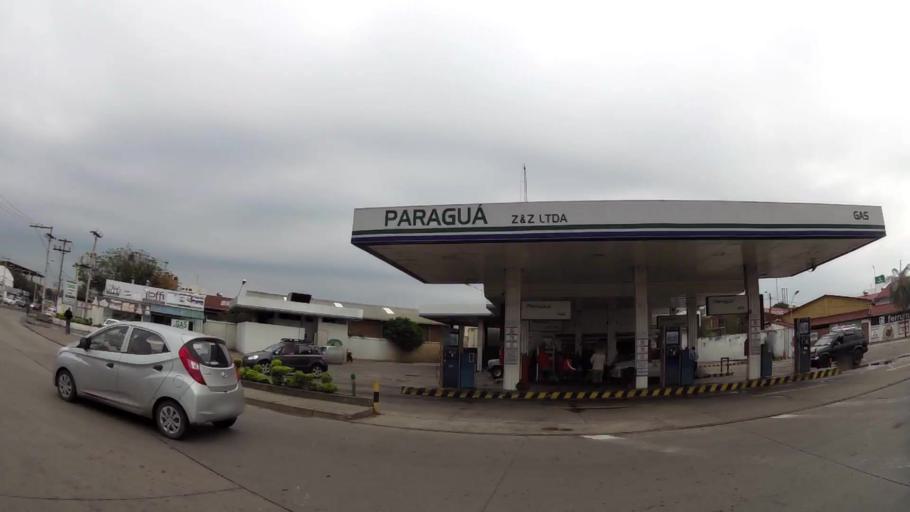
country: BO
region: Santa Cruz
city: Santa Cruz de la Sierra
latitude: -17.7705
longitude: -63.1569
